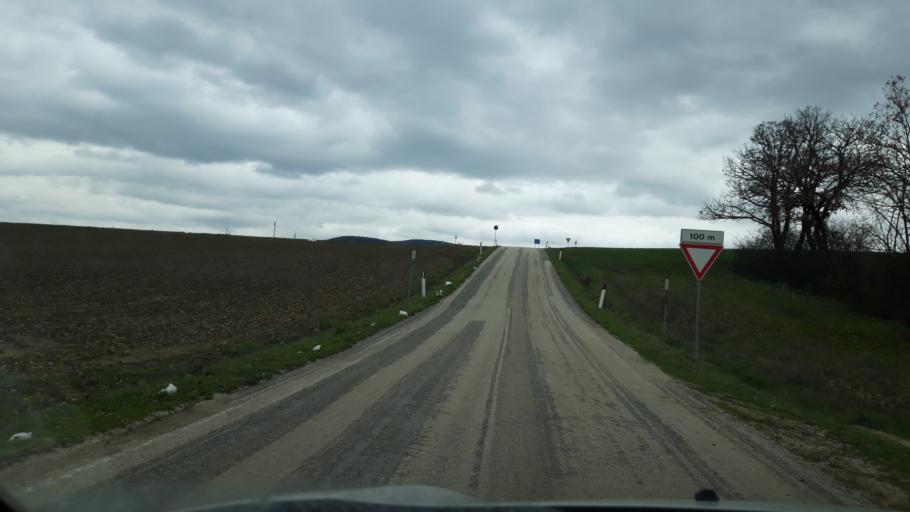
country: IT
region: Umbria
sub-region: Provincia di Perugia
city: Tavernelle
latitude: 42.9880
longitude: 12.1785
